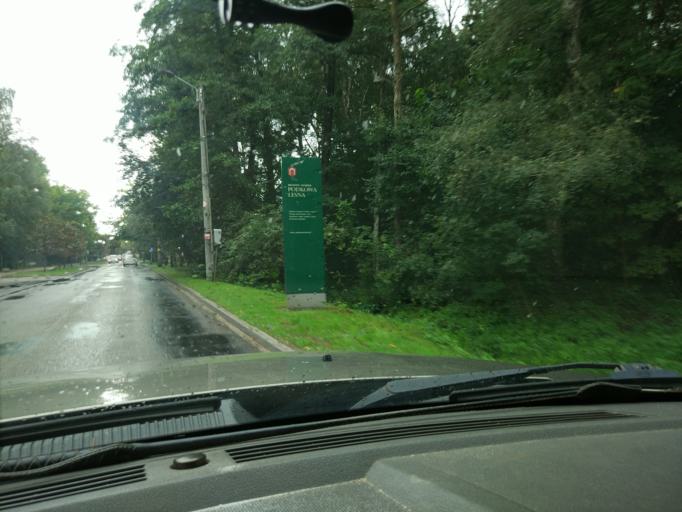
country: PL
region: Masovian Voivodeship
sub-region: Powiat grodziski
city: Podkowa Lesna
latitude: 52.1284
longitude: 20.7184
